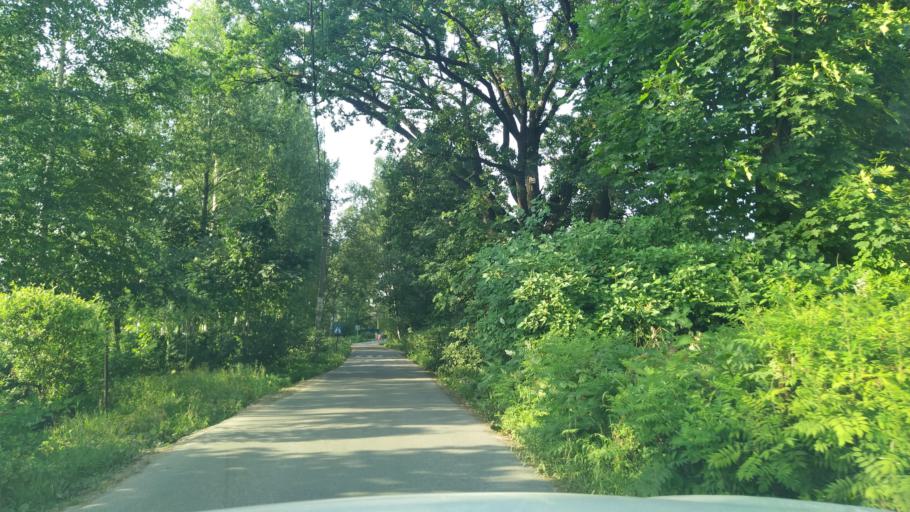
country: RU
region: Leningrad
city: Koltushi
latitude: 59.8940
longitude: 30.7328
